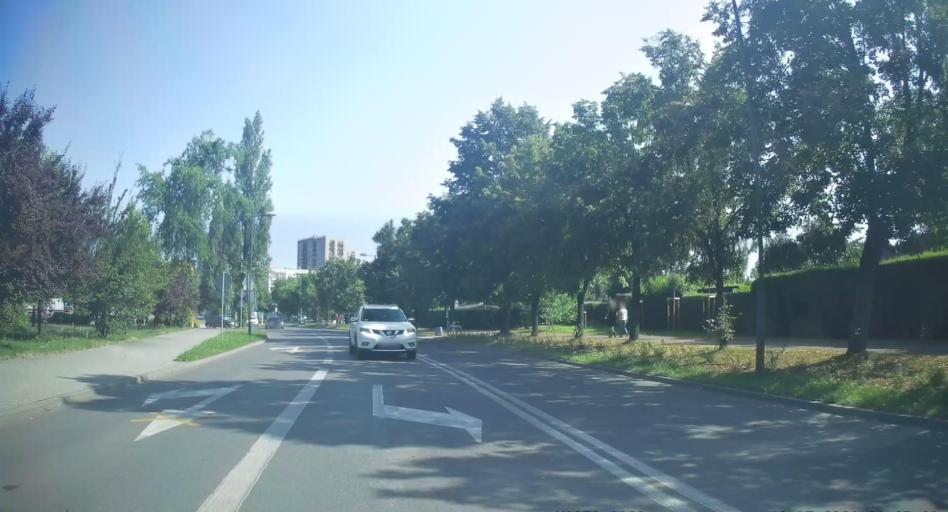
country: PL
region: Silesian Voivodeship
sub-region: Swietochlowice
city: Swietochlowice
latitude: 50.3064
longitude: 18.9131
